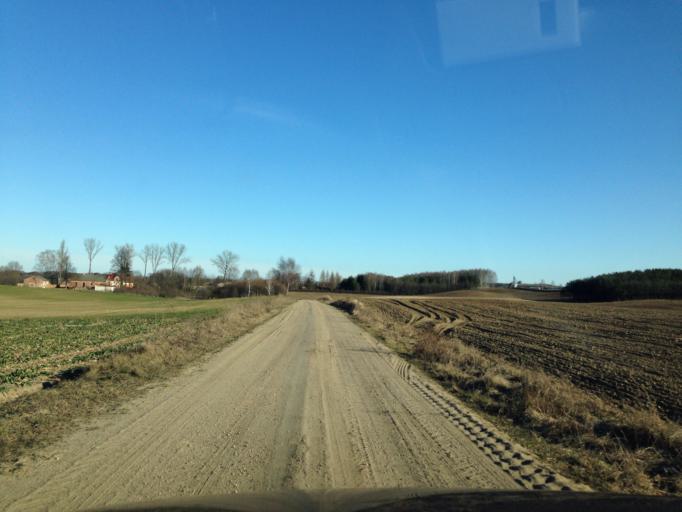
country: PL
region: Kujawsko-Pomorskie
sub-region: Powiat brodnicki
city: Brzozie
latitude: 53.3251
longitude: 19.6591
